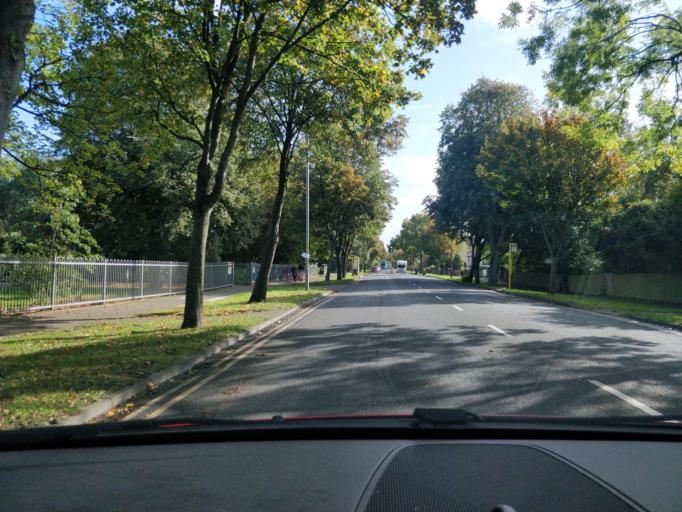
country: GB
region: England
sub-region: Sefton
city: Southport
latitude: 53.6356
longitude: -2.9781
